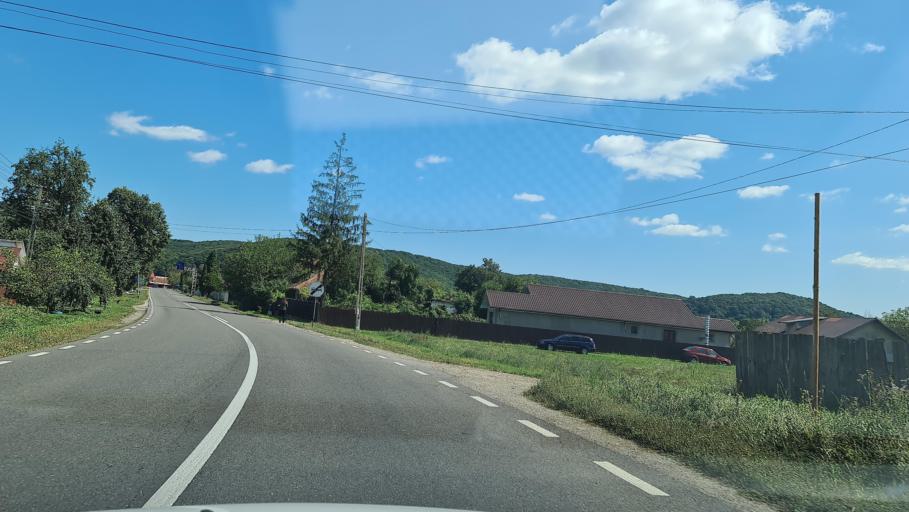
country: RO
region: Bacau
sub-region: Comuna Scorteni
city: Scorteni
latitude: 46.5234
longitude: 26.6602
